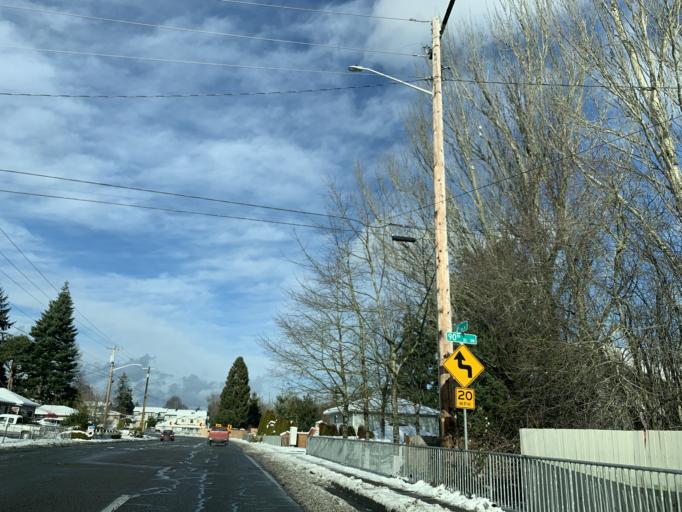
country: US
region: Washington
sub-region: Snohomish County
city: Martha Lake
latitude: 47.9162
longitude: -122.2391
